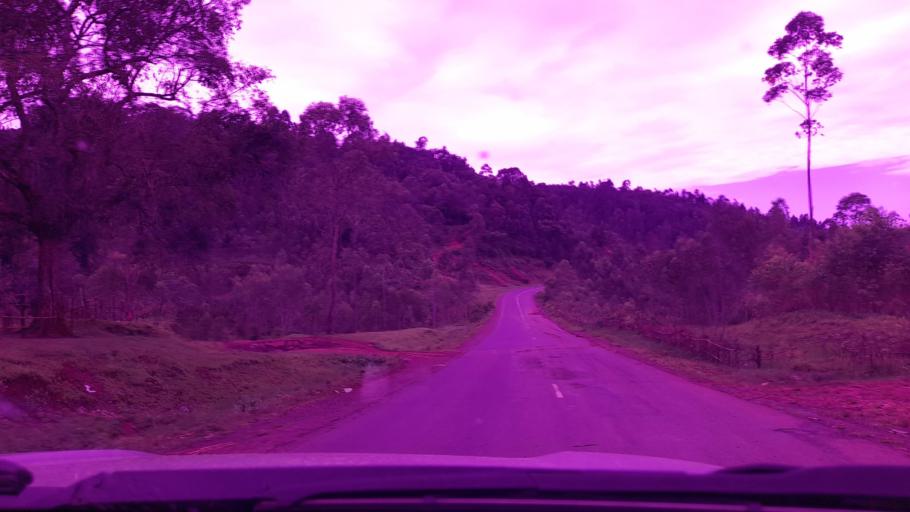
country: ET
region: Southern Nations, Nationalities, and People's Region
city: Mizan Teferi
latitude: 7.0605
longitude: 35.6257
